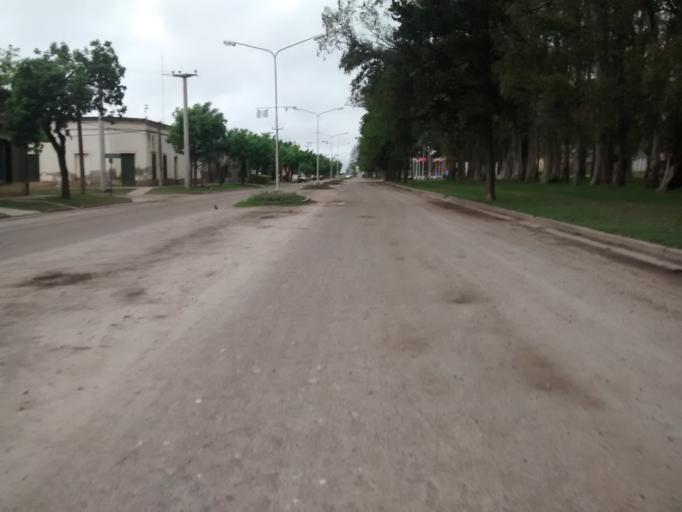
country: AR
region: Santa Fe
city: Galvez
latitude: -31.9034
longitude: -61.2812
